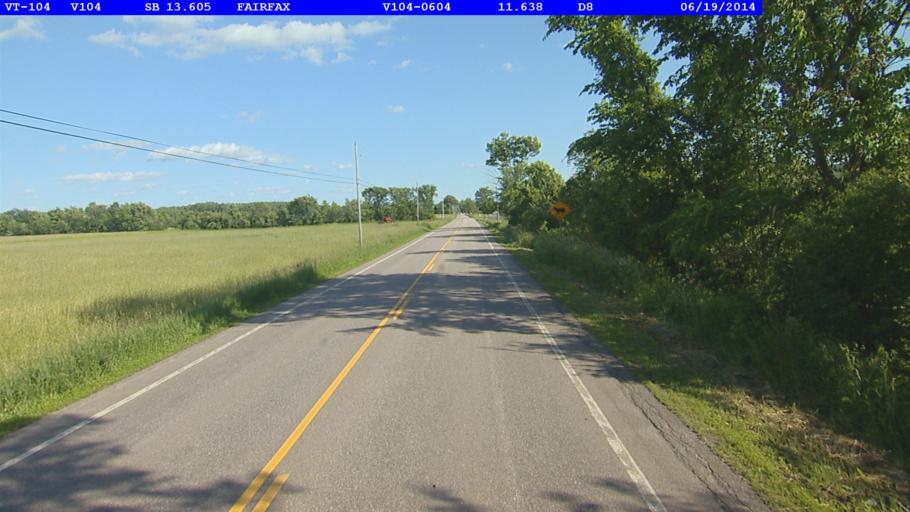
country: US
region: Vermont
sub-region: Franklin County
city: Saint Albans
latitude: 44.7515
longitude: -73.0543
